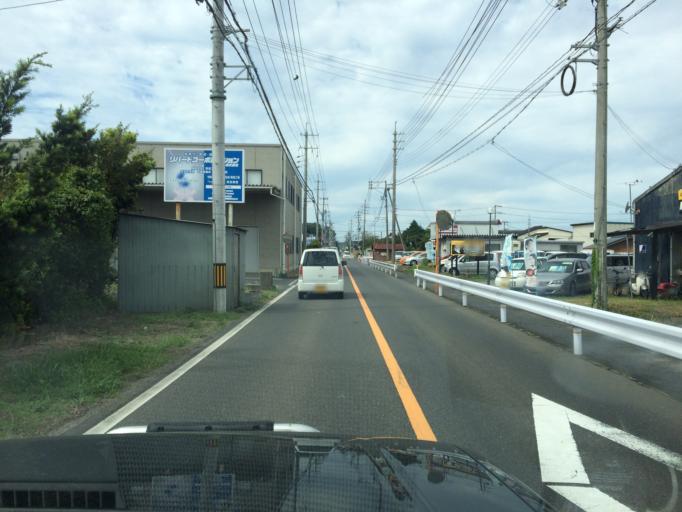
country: JP
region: Tottori
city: Tottori
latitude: 35.5016
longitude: 134.1948
